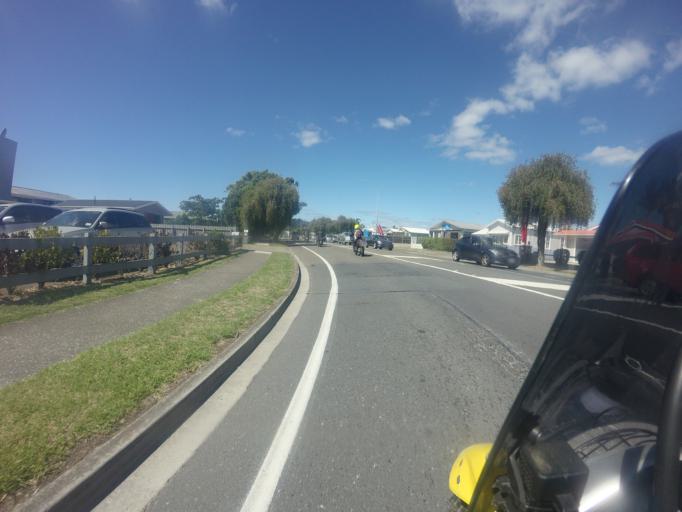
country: NZ
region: Bay of Plenty
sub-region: Whakatane District
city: Whakatane
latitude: -37.9584
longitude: 176.9743
